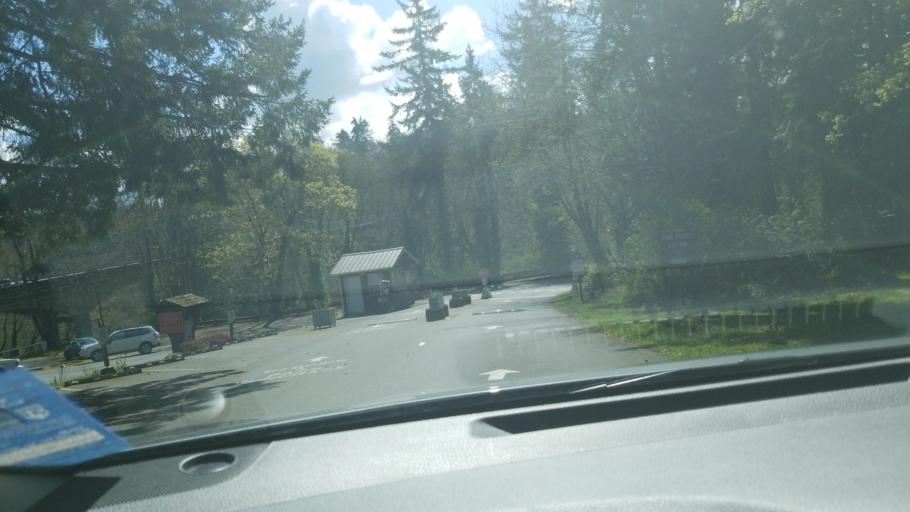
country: US
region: Washington
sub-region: King County
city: Des Moines
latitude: 47.3756
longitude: -122.3227
